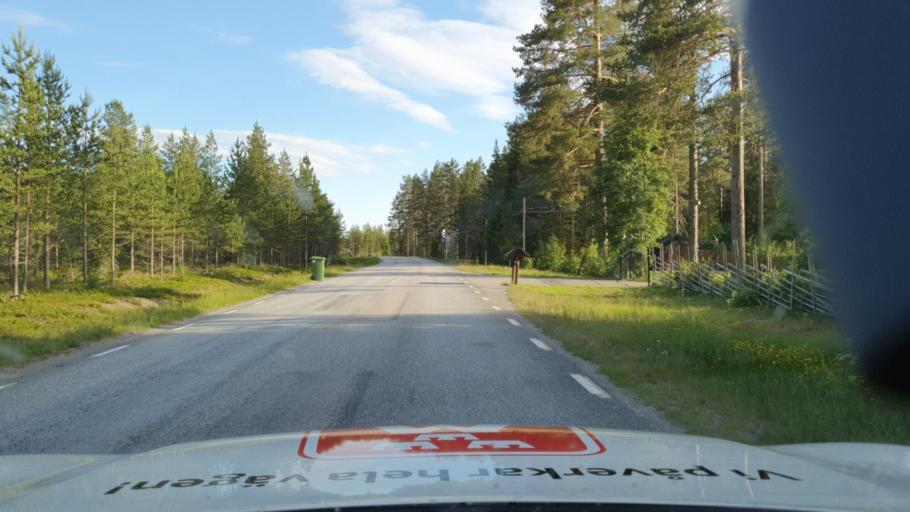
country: SE
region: Vaesterbotten
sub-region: Umea Kommun
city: Roback
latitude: 63.9218
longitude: 20.1449
